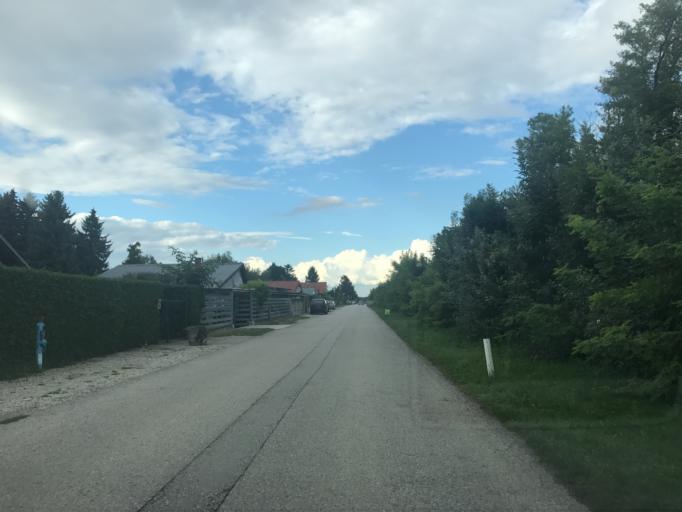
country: AT
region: Burgenland
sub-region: Eisenstadt-Umgebung
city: Neufeld an der Leitha
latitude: 47.8686
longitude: 16.3941
